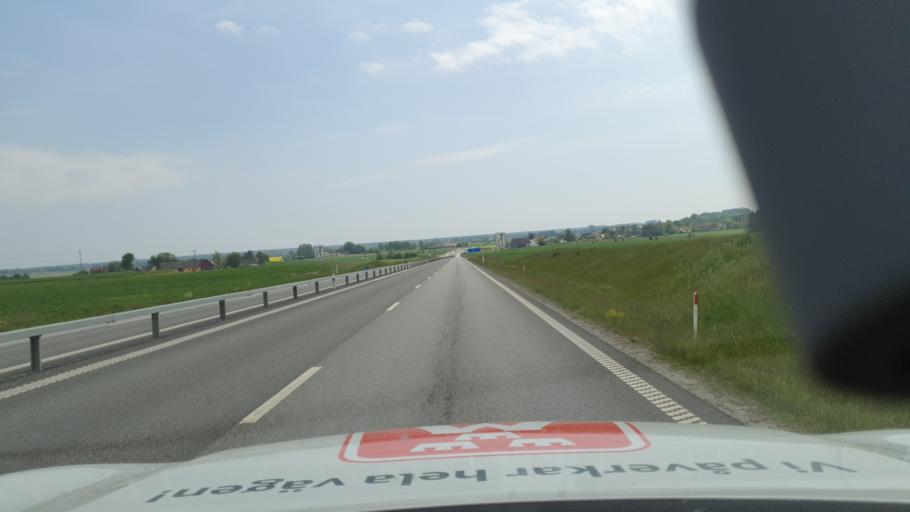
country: SE
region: Skane
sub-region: Ystads Kommun
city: Kopingebro
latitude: 55.4830
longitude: 13.8854
